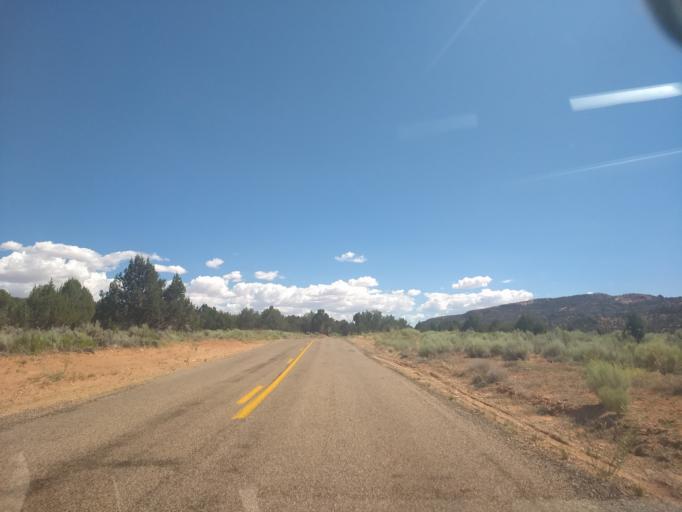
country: US
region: Utah
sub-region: Washington County
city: Hildale
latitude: 36.9968
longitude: -112.8632
